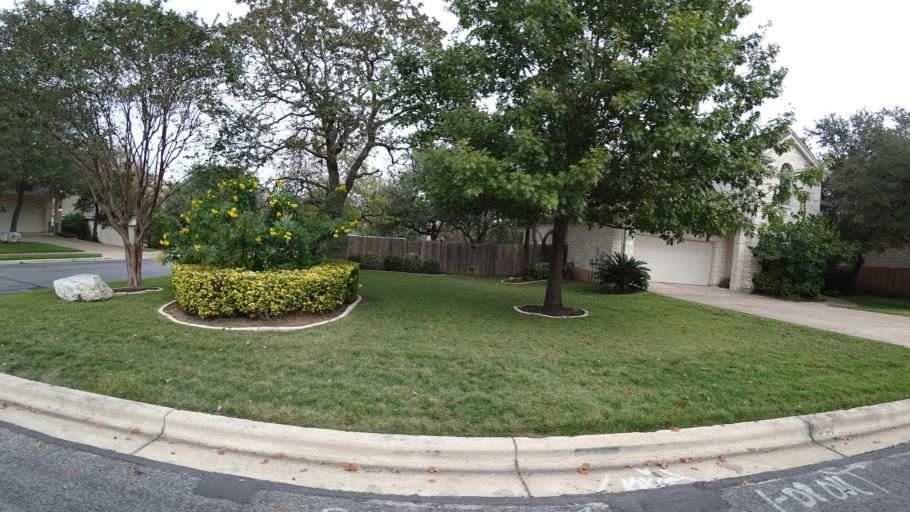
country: US
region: Texas
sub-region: Travis County
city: Shady Hollow
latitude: 30.1928
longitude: -97.8961
